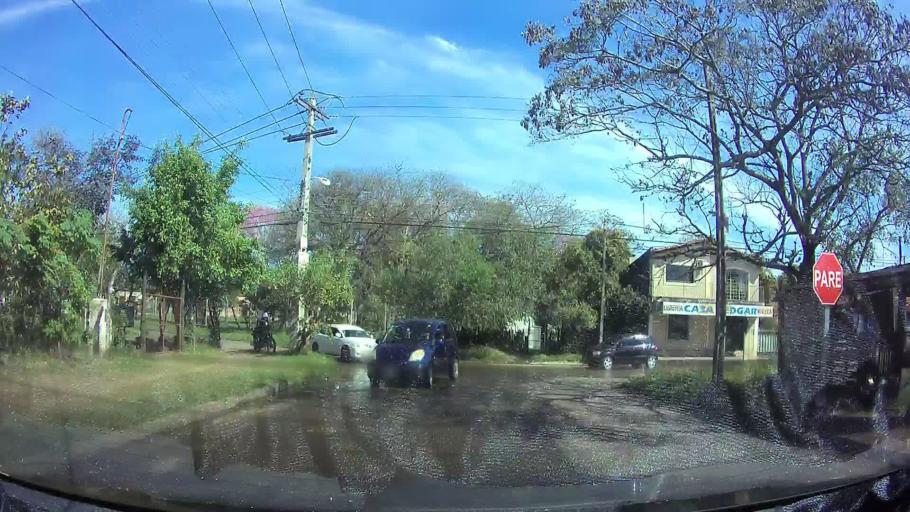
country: PY
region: Central
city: Colonia Mariano Roque Alonso
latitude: -25.2217
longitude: -57.5249
